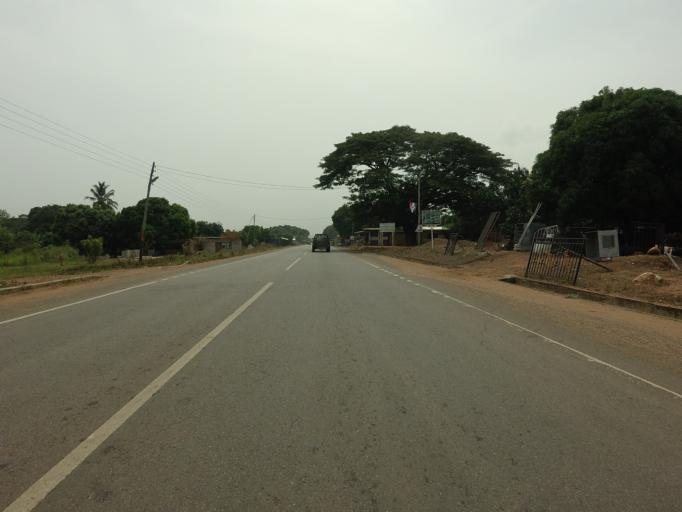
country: GH
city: Akropong
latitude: 6.0739
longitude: -0.0183
